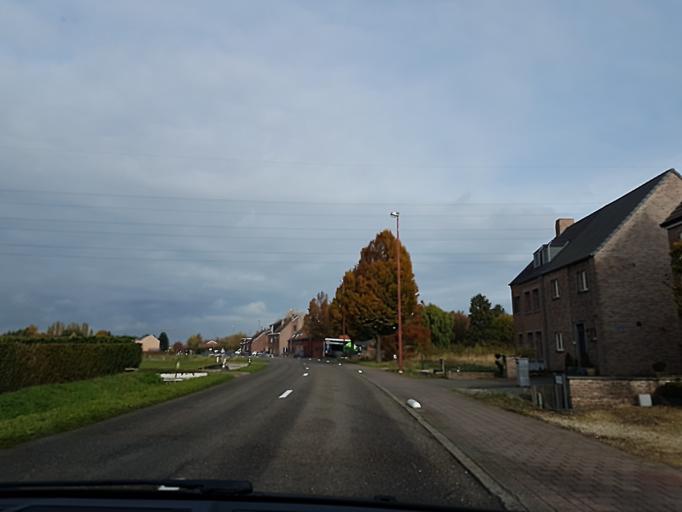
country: BE
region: Flanders
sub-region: Provincie Antwerpen
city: Lint
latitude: 51.1163
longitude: 4.4950
